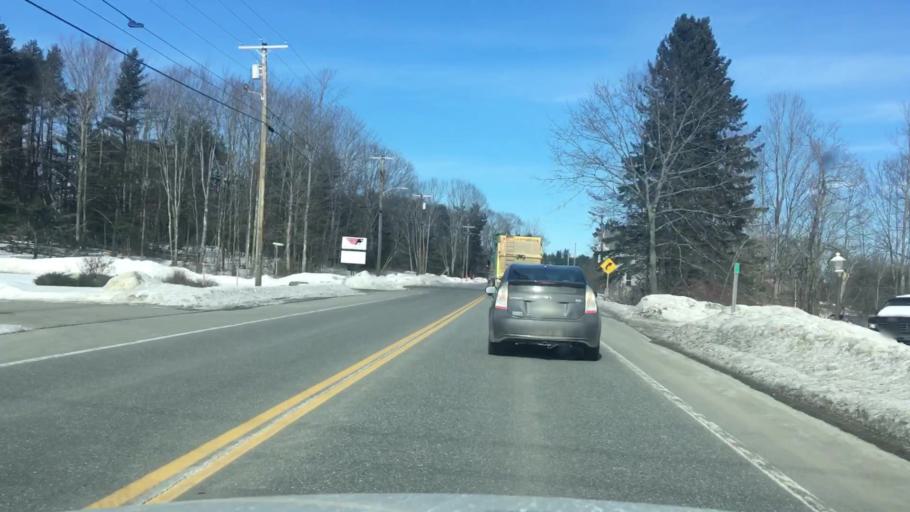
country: US
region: Maine
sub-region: Penobscot County
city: Orrington
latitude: 44.7366
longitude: -68.8210
